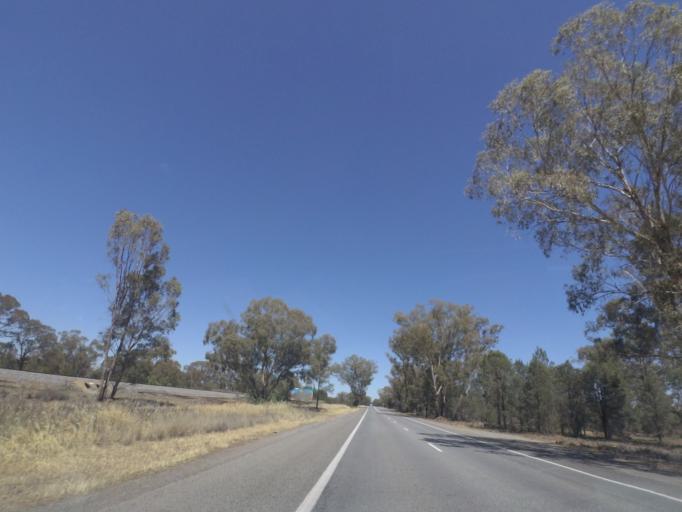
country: AU
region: New South Wales
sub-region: Narrandera
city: Narrandera
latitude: -34.7377
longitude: 146.5840
